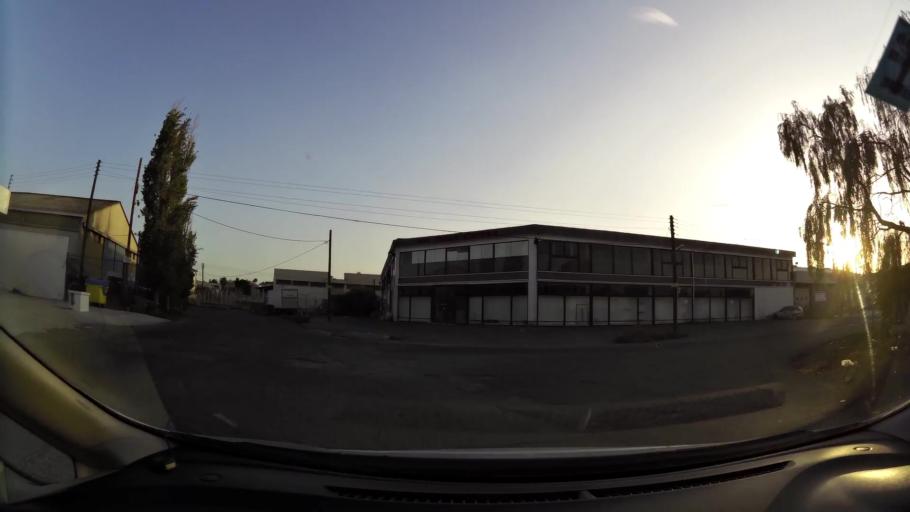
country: CY
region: Lefkosia
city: Nicosia
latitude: 35.1670
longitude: 33.3220
